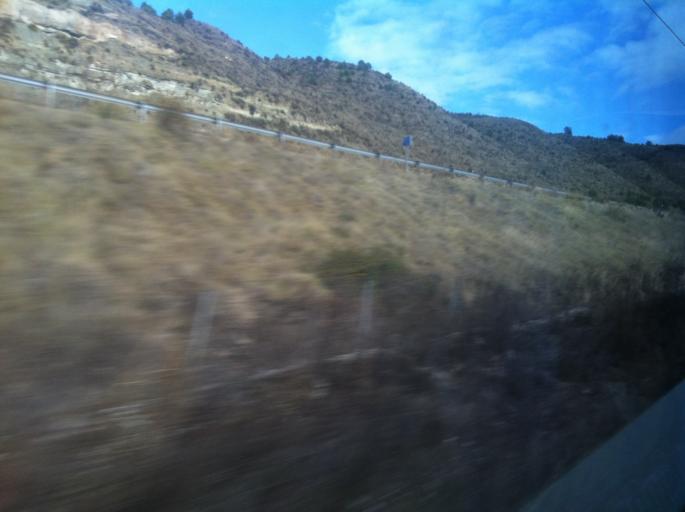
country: ES
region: Castille and Leon
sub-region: Provincia de Burgos
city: Castil de Peones
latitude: 42.4945
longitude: -3.3713
